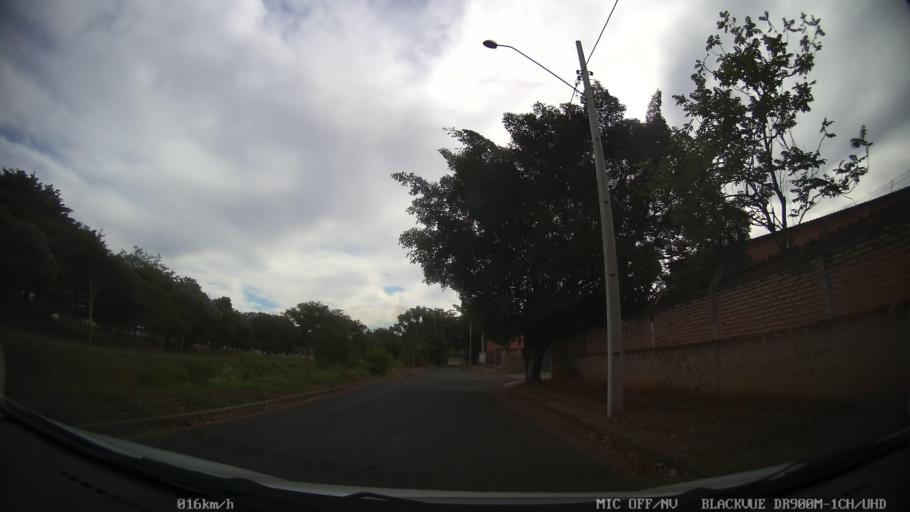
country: BR
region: Sao Paulo
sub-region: Catanduva
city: Catanduva
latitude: -21.1255
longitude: -48.9832
